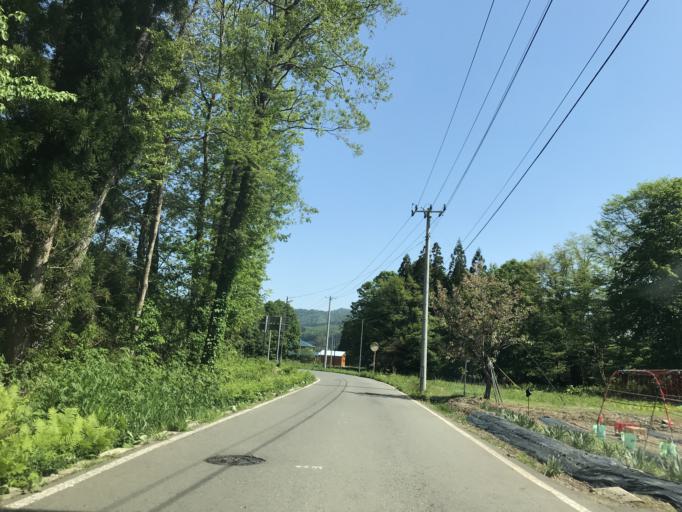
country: JP
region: Iwate
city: Shizukuishi
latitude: 39.5603
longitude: 140.8406
